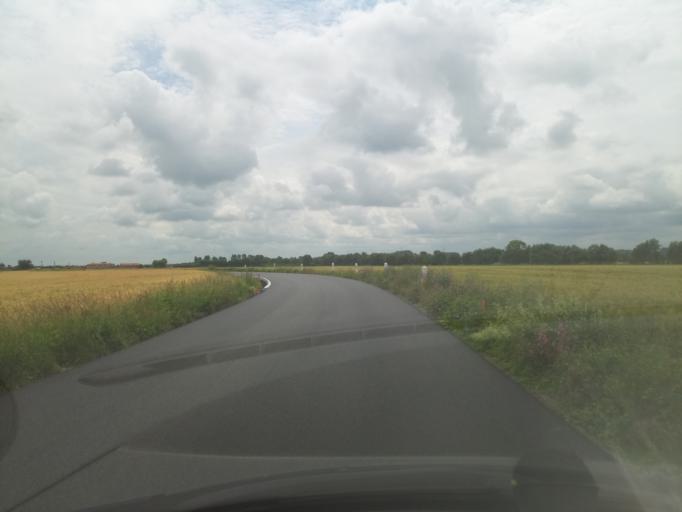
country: FR
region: Poitou-Charentes
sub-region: Departement de la Charente-Maritime
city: Saint-Jean-de-Liversay
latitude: 46.2726
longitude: -0.9026
